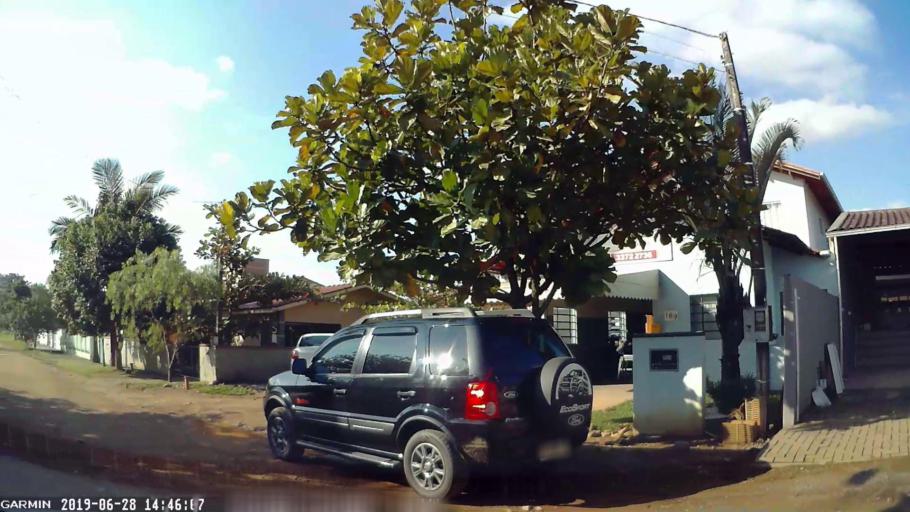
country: BR
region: Santa Catarina
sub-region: Schroeder
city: Schroeder
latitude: -26.4521
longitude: -49.1332
